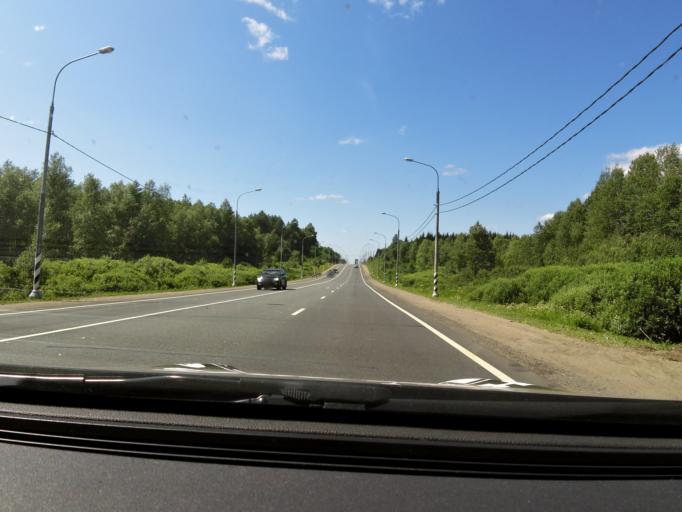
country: RU
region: Novgorod
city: Valday
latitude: 57.9937
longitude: 33.1842
